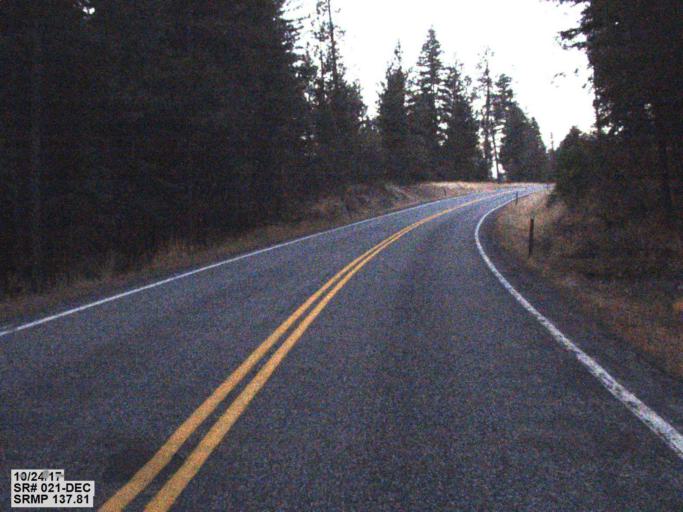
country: US
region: Washington
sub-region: Ferry County
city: Republic
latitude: 48.3596
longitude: -118.7408
